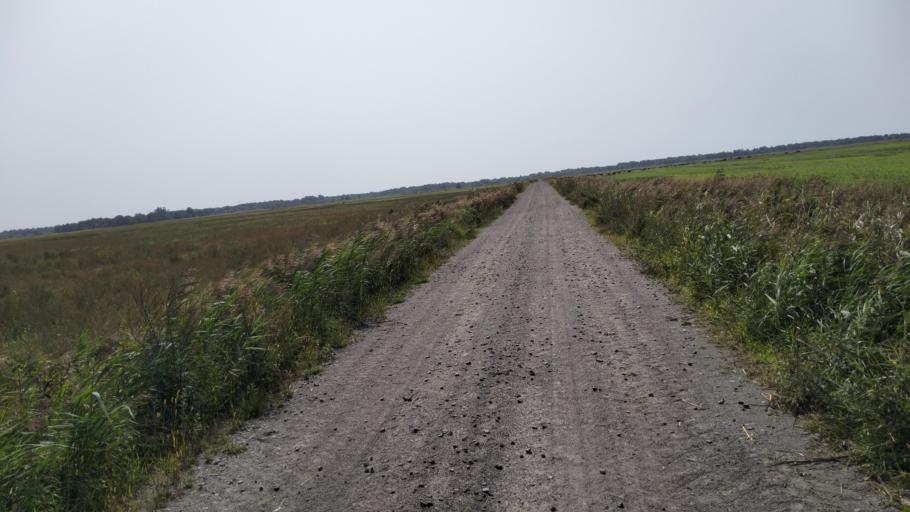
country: BY
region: Brest
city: Davyd-Haradok
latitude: 51.9849
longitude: 27.1753
